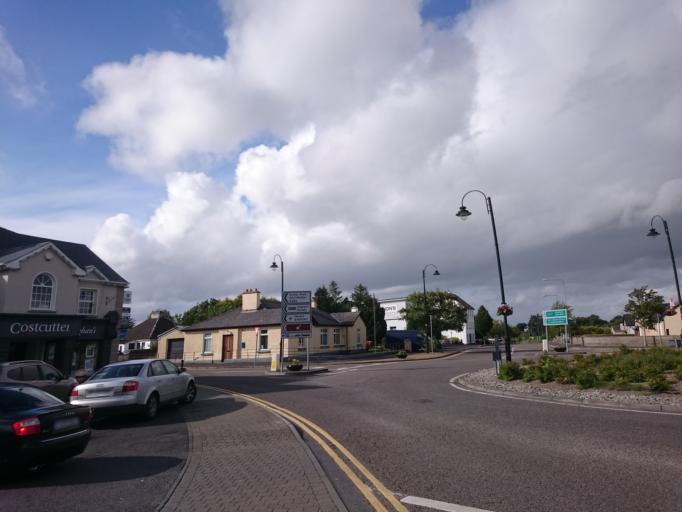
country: IE
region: Connaught
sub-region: Maigh Eo
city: Kiltamagh
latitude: 53.7949
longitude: -8.9188
